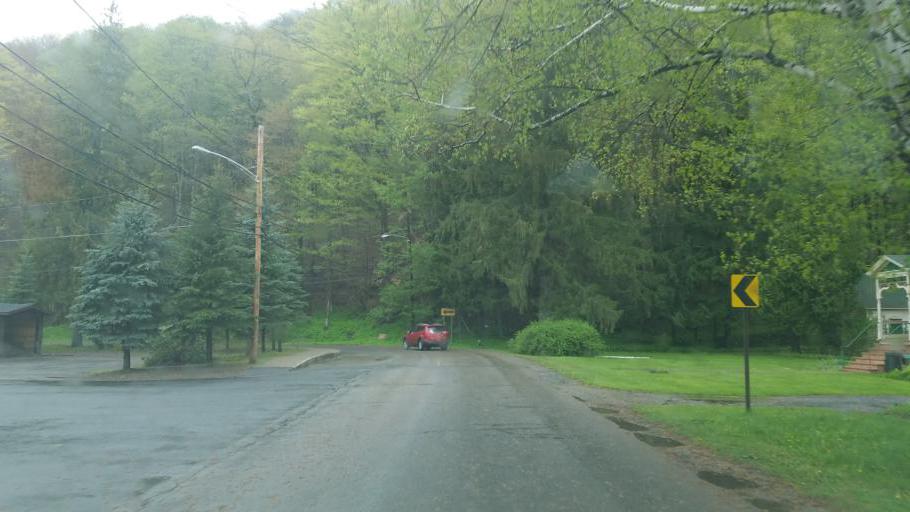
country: US
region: Pennsylvania
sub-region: Potter County
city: Coudersport
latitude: 41.7729
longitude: -78.0228
